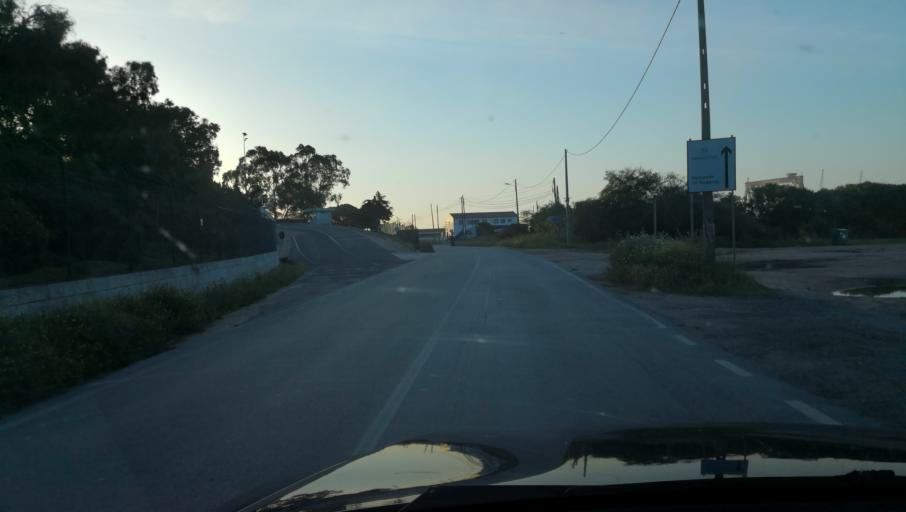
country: PT
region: Setubal
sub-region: Setubal
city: Setubal
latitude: 38.4887
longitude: -8.8100
